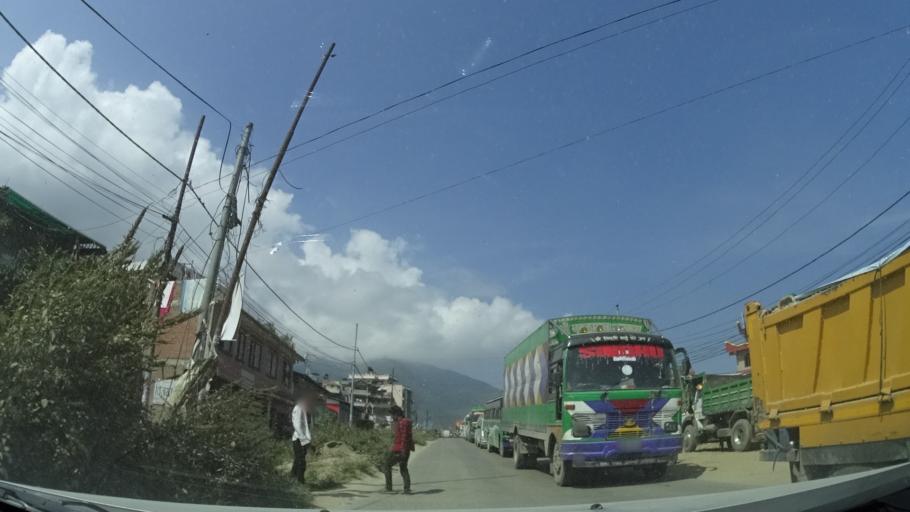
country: NP
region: Central Region
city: Kirtipur
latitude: 27.6884
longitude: 85.2346
